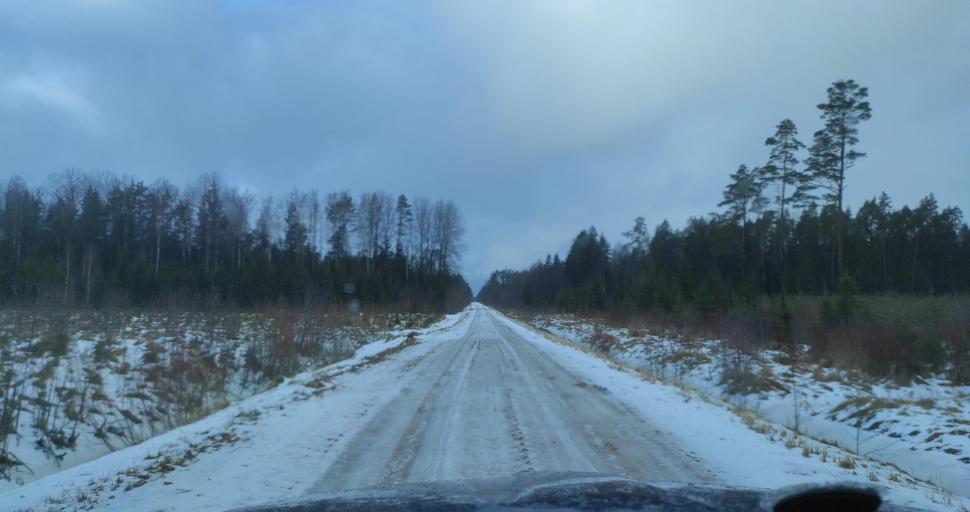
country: LV
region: Dundaga
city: Dundaga
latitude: 57.4039
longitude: 22.0990
